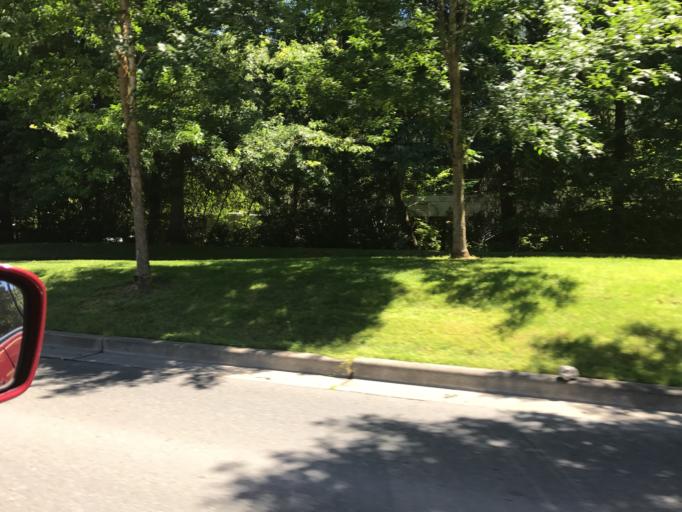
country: US
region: Washington
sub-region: King County
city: Redmond
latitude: 47.6415
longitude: -122.1322
